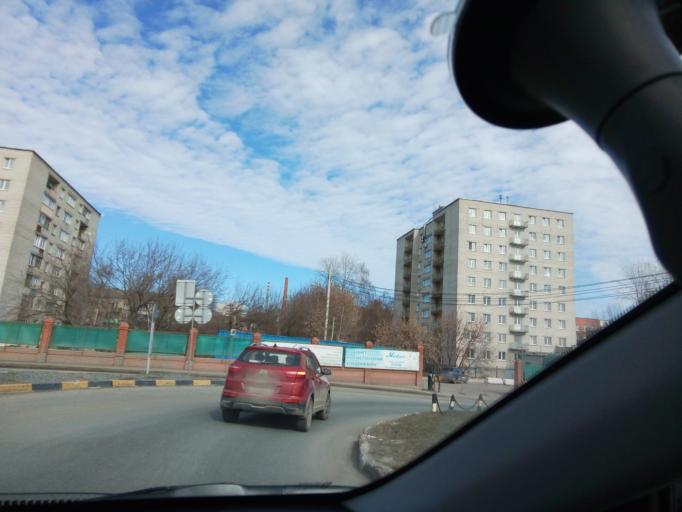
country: RU
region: Chuvashia
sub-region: Cheboksarskiy Rayon
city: Cheboksary
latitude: 56.1238
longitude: 47.2455
